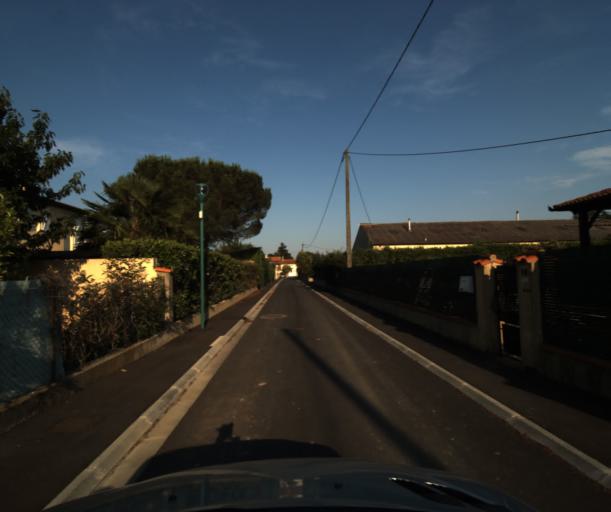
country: FR
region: Midi-Pyrenees
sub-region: Departement de la Haute-Garonne
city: Roquettes
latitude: 43.4810
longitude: 1.3815
